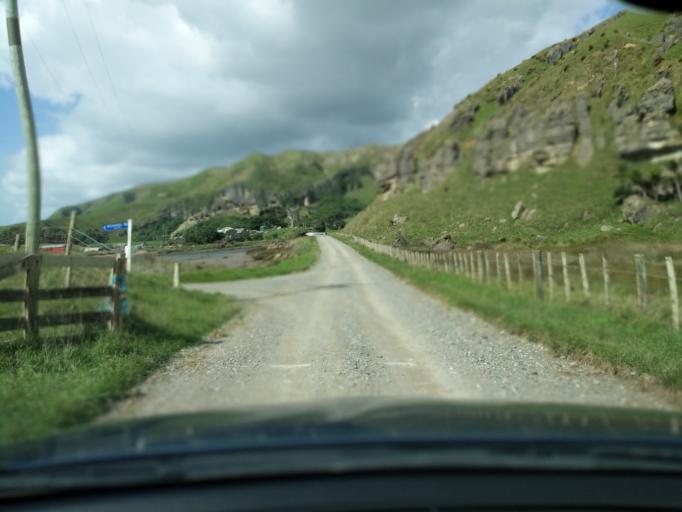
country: NZ
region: Tasman
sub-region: Tasman District
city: Takaka
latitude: -40.6461
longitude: 172.4309
